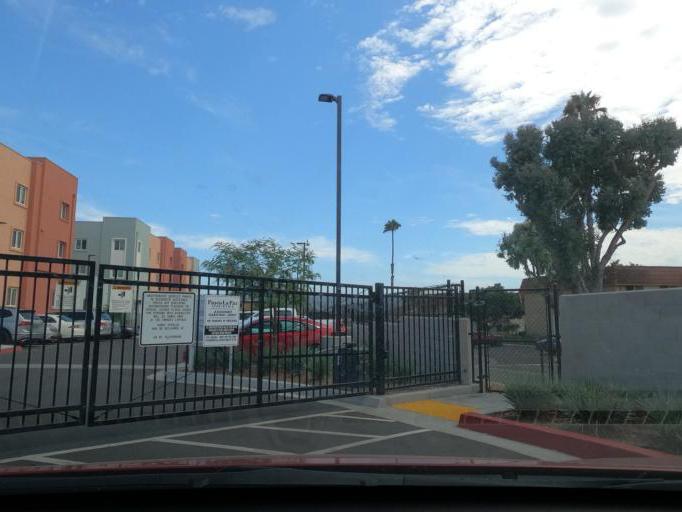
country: MX
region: Baja California
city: Tijuana
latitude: 32.5567
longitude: -117.0464
